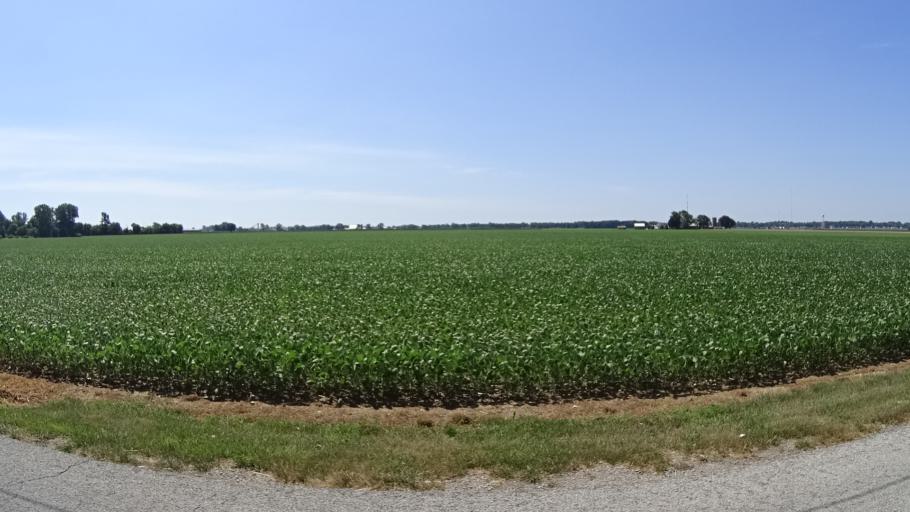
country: US
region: Ohio
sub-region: Erie County
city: Sandusky
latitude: 41.4256
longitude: -82.7835
